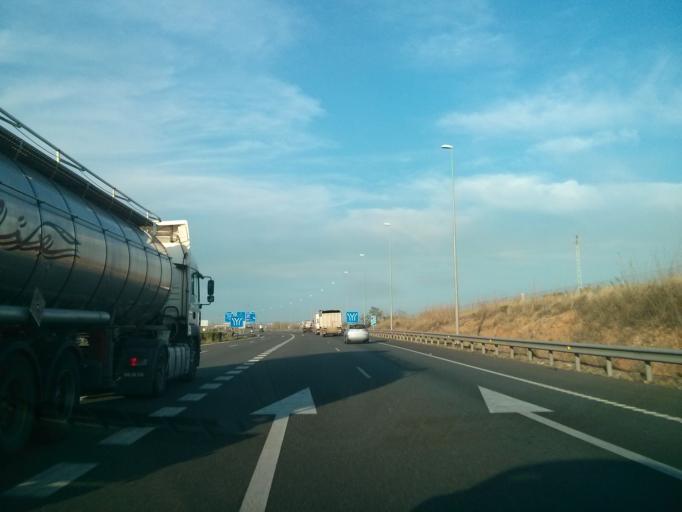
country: ES
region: Valencia
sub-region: Provincia de Valencia
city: Sagunto
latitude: 39.6966
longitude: -0.2755
